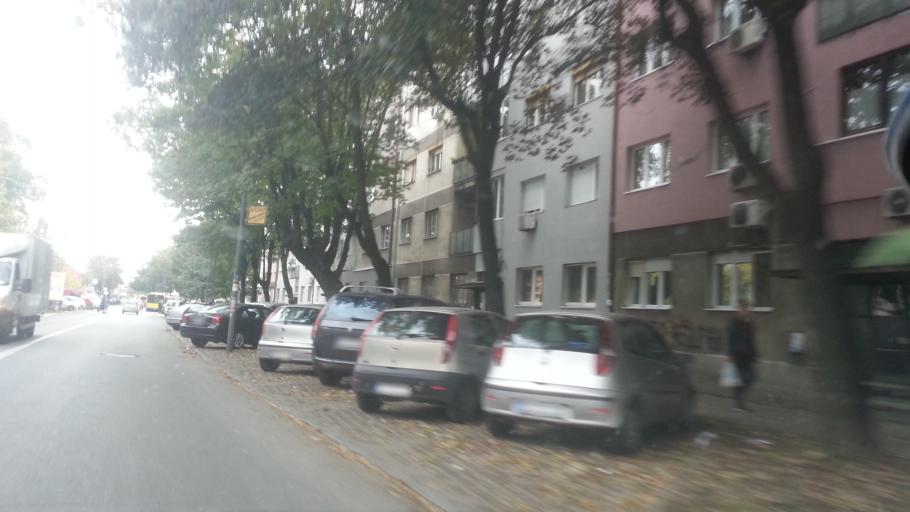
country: RS
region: Central Serbia
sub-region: Belgrade
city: Zemun
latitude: 44.8411
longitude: 20.3938
